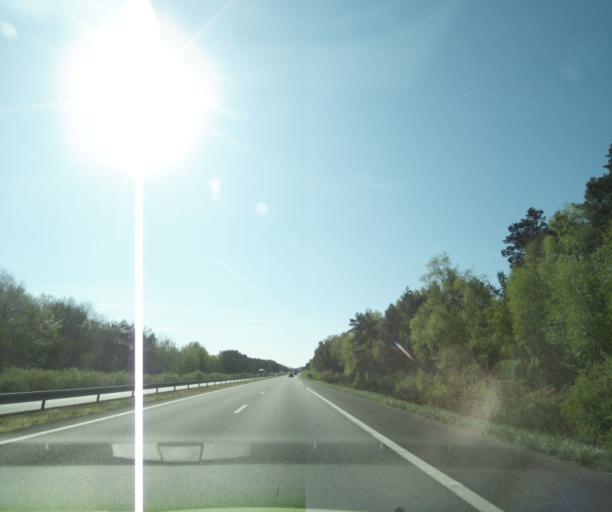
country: FR
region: Centre
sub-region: Departement du Loir-et-Cher
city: Chaumont-sur-Tharonne
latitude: 47.6600
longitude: 1.9315
